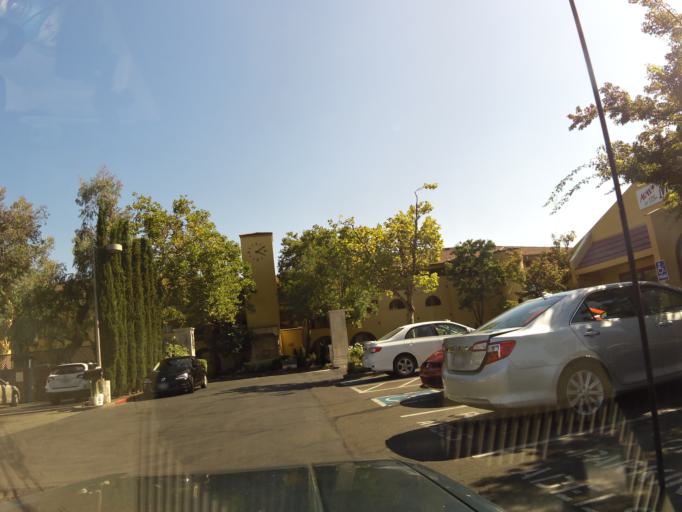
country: US
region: California
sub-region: Sonoma County
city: Healdsburg
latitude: 38.6260
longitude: -122.8765
